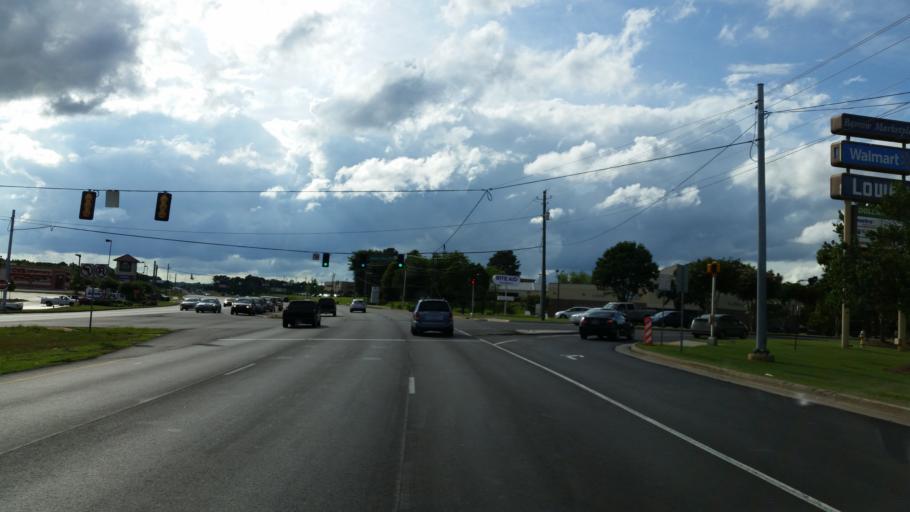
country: US
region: Georgia
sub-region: Bartow County
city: Cartersville
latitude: 34.1983
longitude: -84.7919
